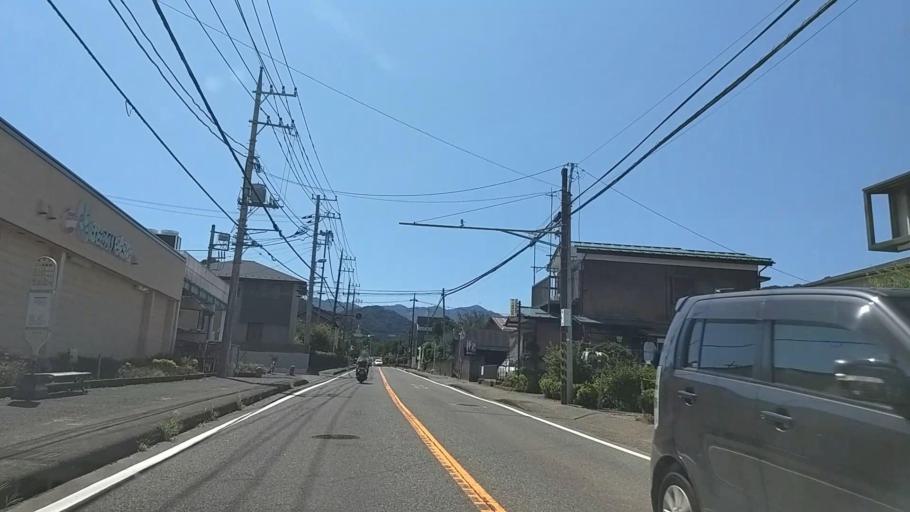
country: JP
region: Tokyo
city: Hachioji
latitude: 35.5856
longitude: 139.2311
